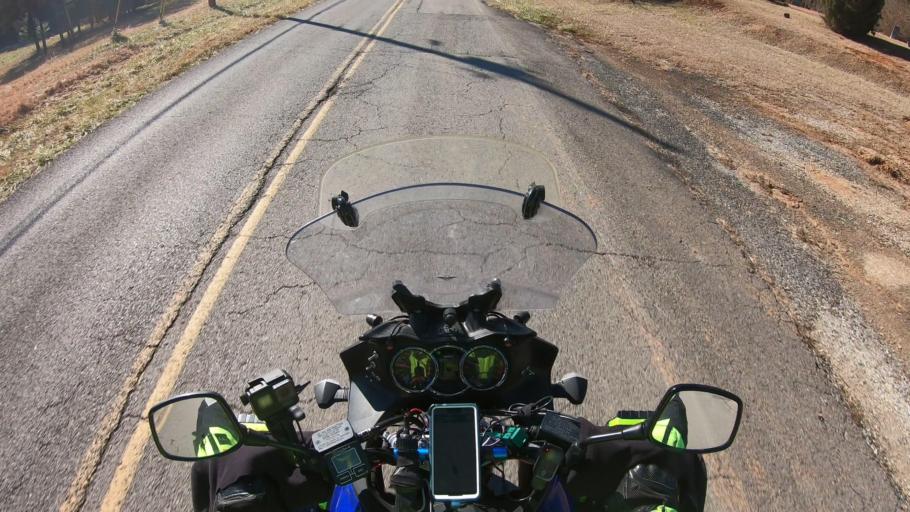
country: US
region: Georgia
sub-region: Fannin County
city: McCaysville
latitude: 34.9969
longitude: -84.3357
